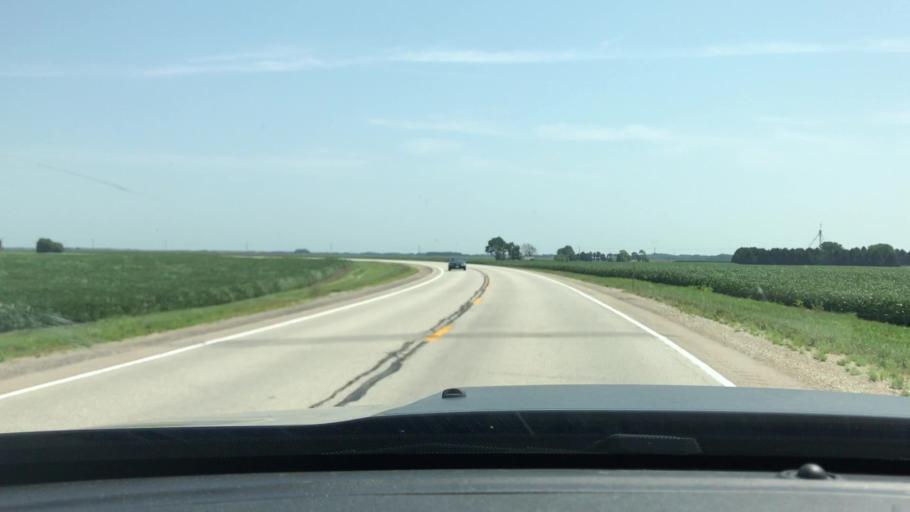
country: US
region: Illinois
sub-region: LaSalle County
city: Ottawa
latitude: 41.4708
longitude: -88.8228
